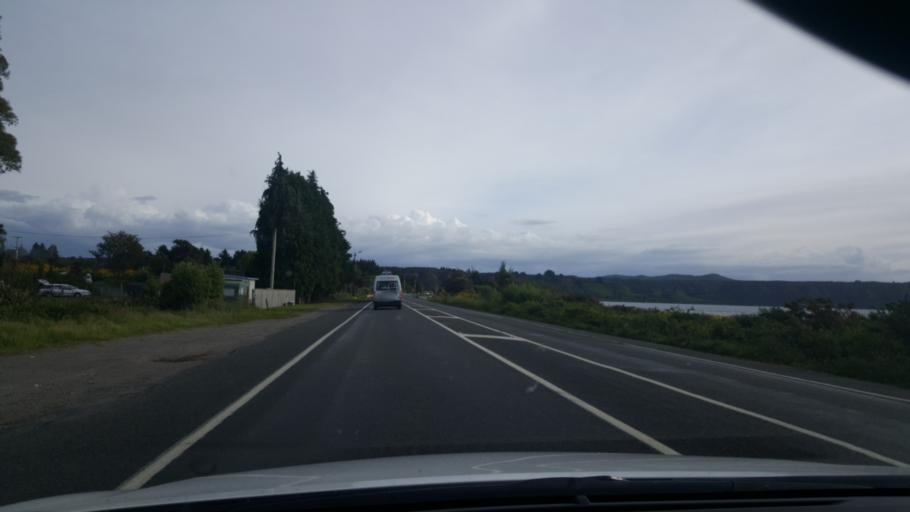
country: NZ
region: Waikato
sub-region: Taupo District
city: Taupo
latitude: -38.7833
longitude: 176.0769
